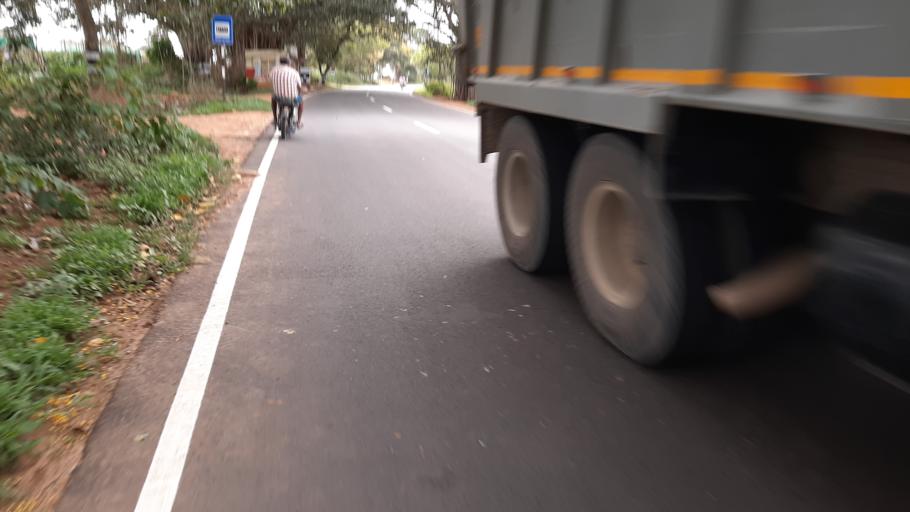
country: IN
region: Tamil Nadu
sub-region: Krishnagiri
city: Denkanikota
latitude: 12.5369
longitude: 77.7710
